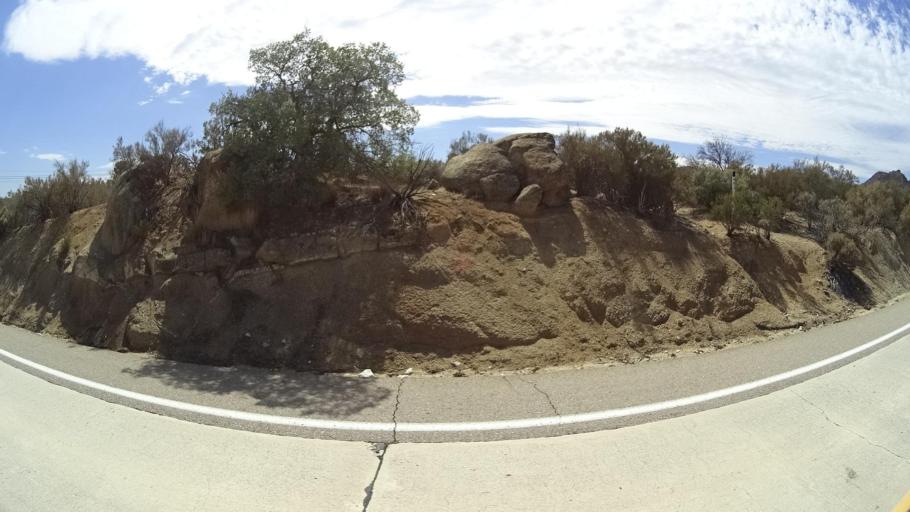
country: MX
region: Baja California
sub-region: Tecate
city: Cereso del Hongo
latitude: 32.6225
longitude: -116.2186
